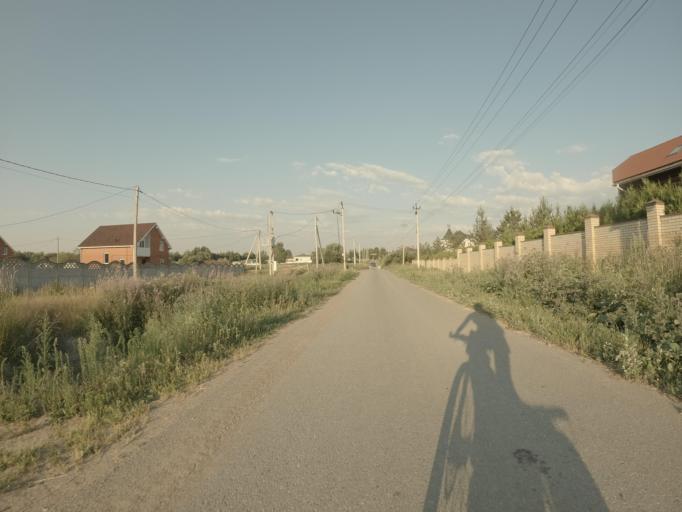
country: RU
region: Leningrad
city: Koltushi
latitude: 59.8891
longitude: 30.7008
